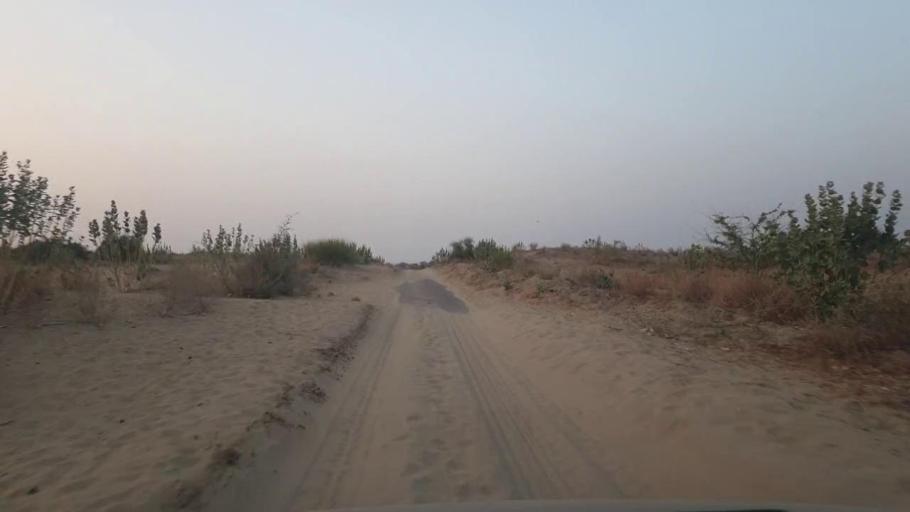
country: PK
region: Sindh
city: Umarkot
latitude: 25.3028
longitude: 70.0724
